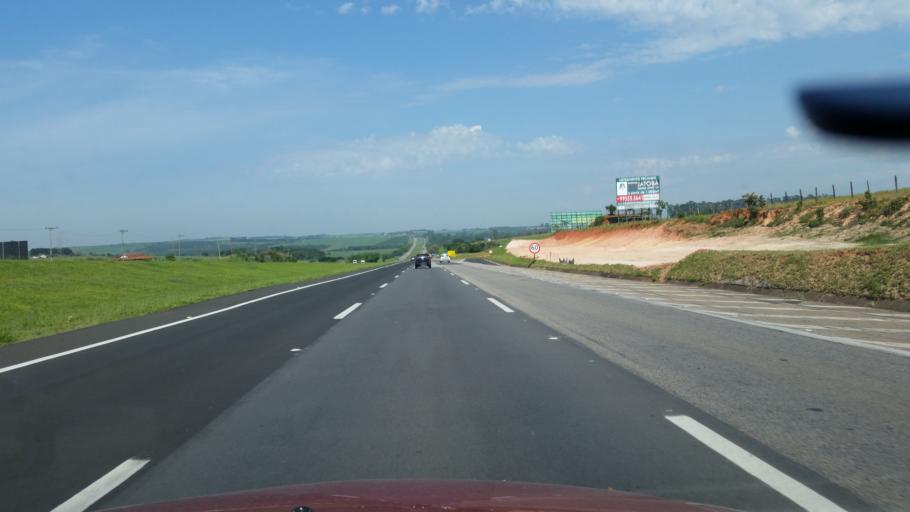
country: BR
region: Sao Paulo
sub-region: Boituva
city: Boituva
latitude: -23.2911
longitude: -47.7398
